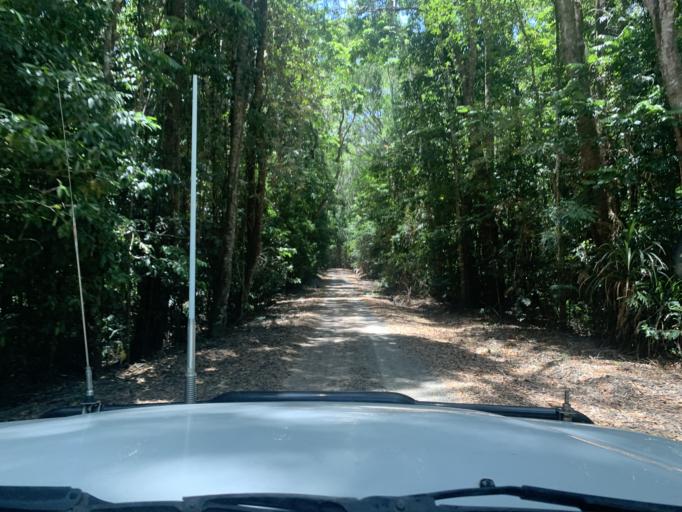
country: AU
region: Queensland
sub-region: Cairns
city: Redlynch
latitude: -16.9499
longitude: 145.6346
